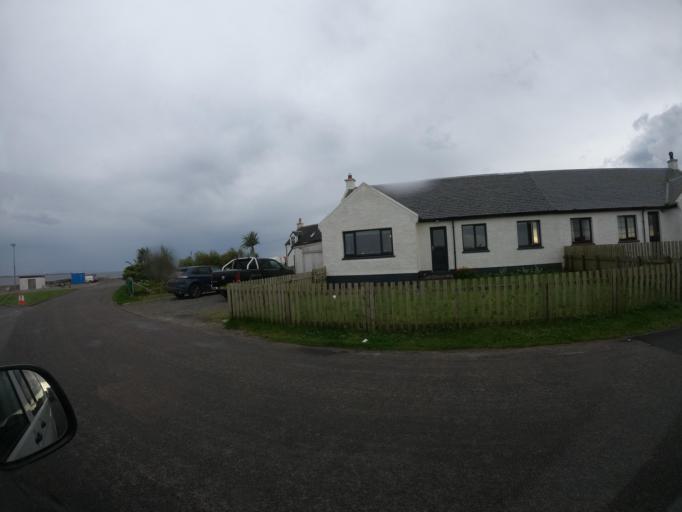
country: GB
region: Scotland
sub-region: Eilean Siar
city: Barra
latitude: 56.5080
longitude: -6.8000
